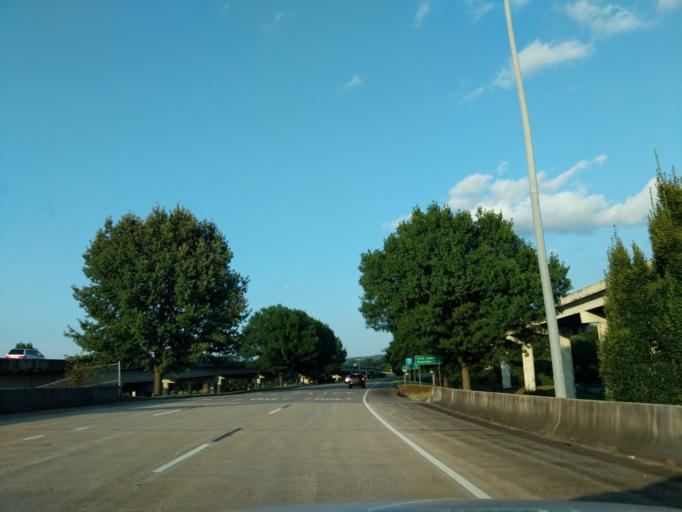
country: US
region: Alabama
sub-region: Madison County
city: Huntsville
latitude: 34.7367
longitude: -86.5921
